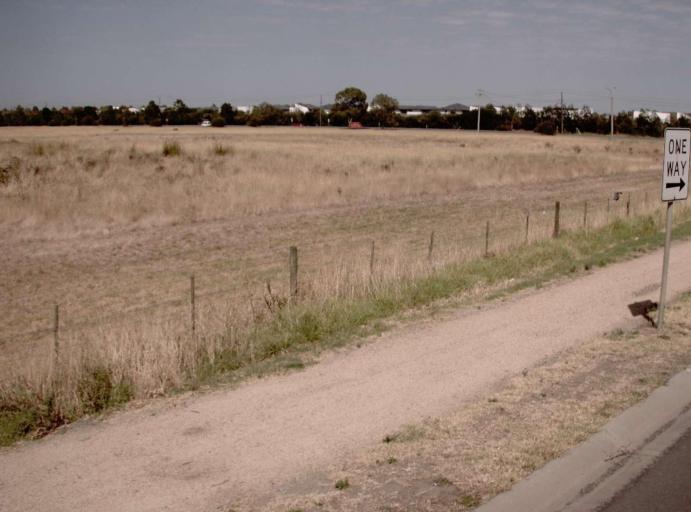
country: AU
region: Victoria
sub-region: Kingston
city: Waterways
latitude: -38.0111
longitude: 145.1429
